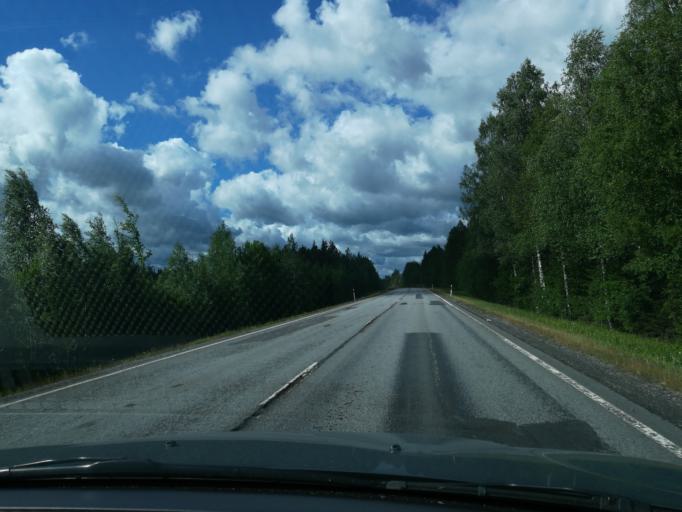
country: FI
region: Southern Savonia
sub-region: Mikkeli
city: Ristiina
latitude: 61.4312
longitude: 27.2357
